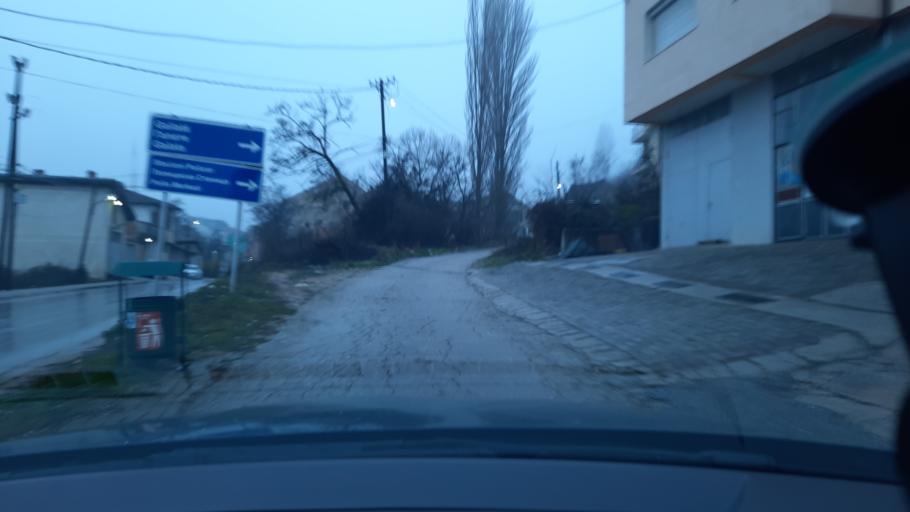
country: MK
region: Vrapciste
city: Vrapciste
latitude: 41.8393
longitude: 20.8848
